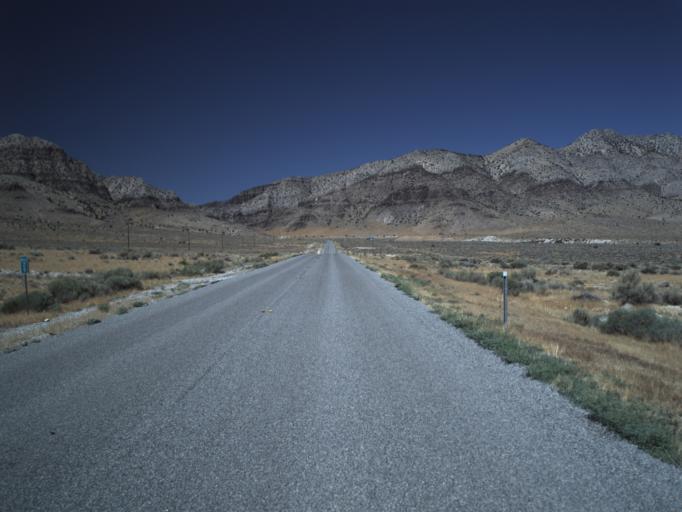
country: US
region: Utah
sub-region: Beaver County
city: Milford
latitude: 39.0863
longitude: -113.5306
